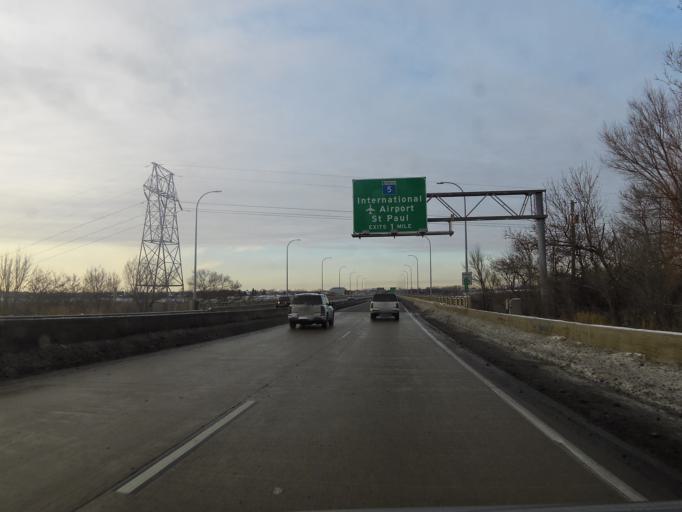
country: US
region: Minnesota
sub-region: Dakota County
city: Mendota Heights
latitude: 44.8840
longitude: -93.1709
